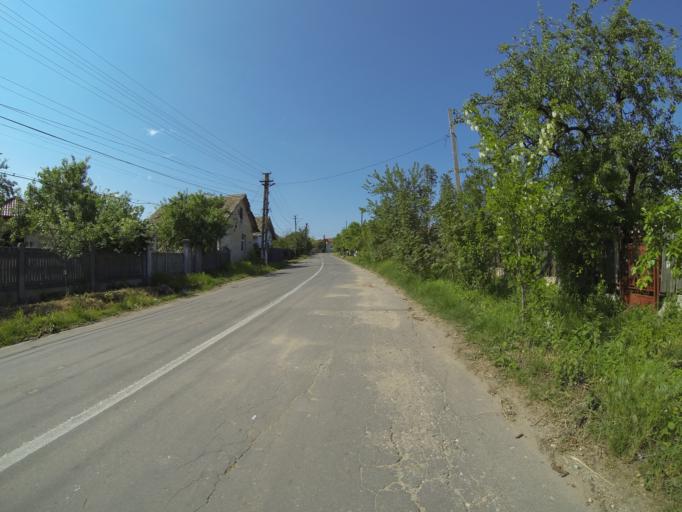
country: RO
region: Dolj
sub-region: Comuna Plenita
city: Plenita
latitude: 44.2230
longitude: 23.1790
